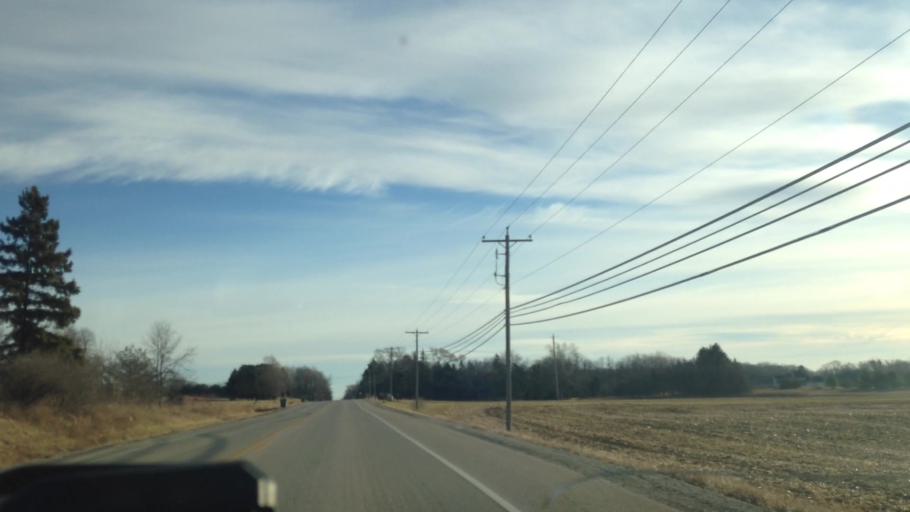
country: US
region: Wisconsin
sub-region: Ozaukee County
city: Cedarburg
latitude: 43.2932
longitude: -88.0333
